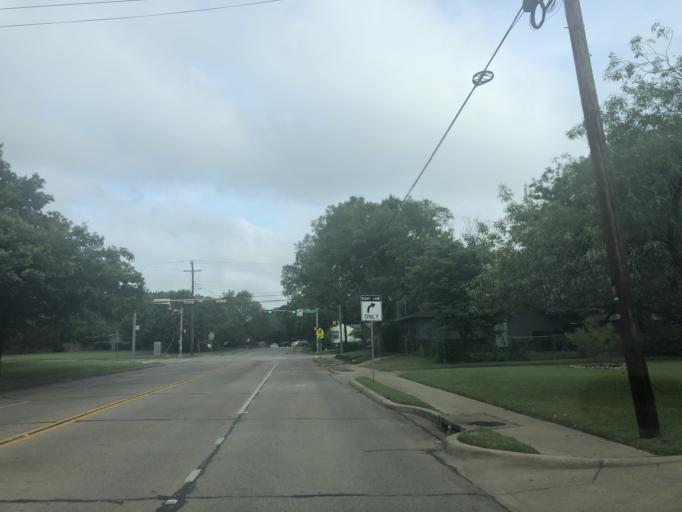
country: US
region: Texas
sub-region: Dallas County
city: Irving
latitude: 32.8097
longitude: -96.9757
